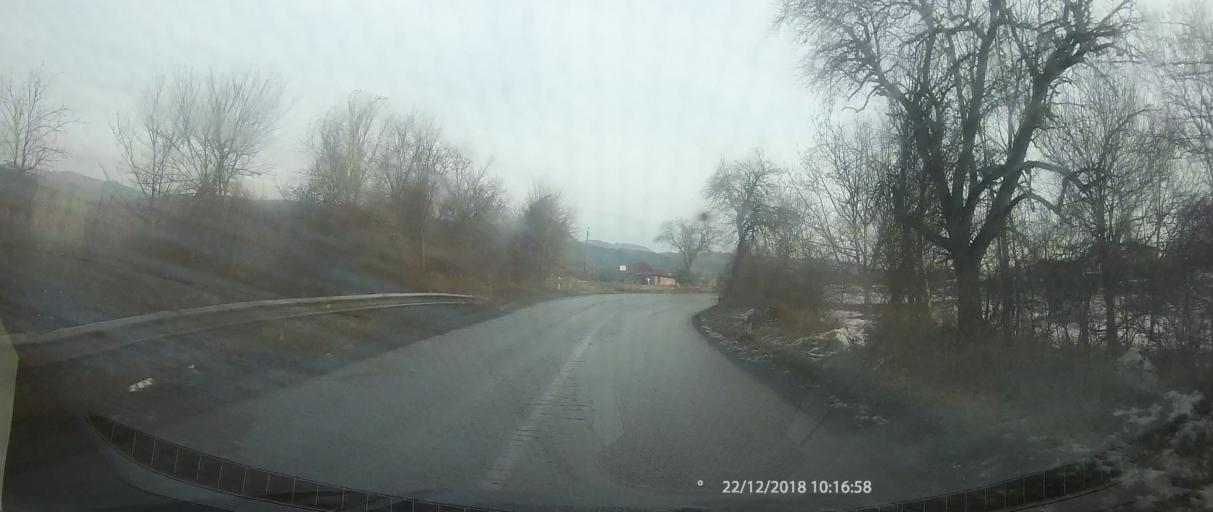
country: MK
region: Kriva Palanka
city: Kriva Palanka
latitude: 42.1803
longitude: 22.2724
